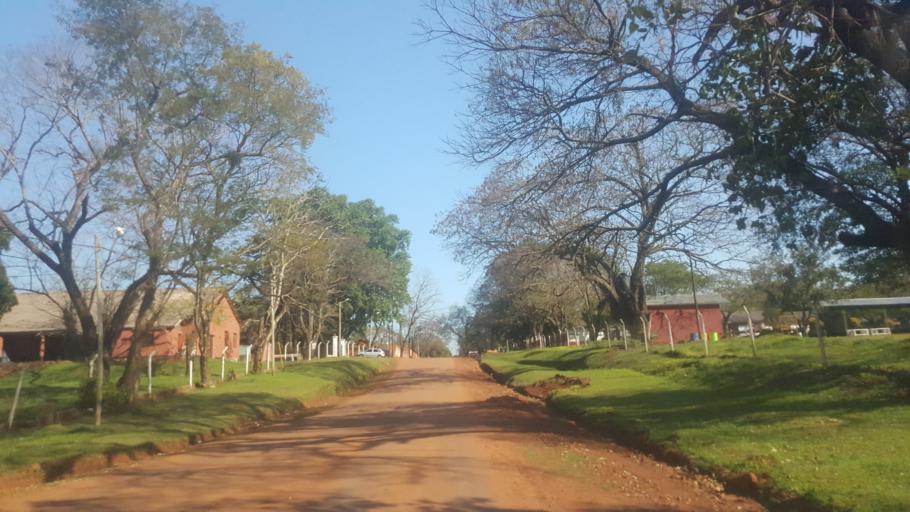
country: AR
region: Misiones
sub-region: Departamento de Capital
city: Posadas
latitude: -27.3626
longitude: -55.9197
